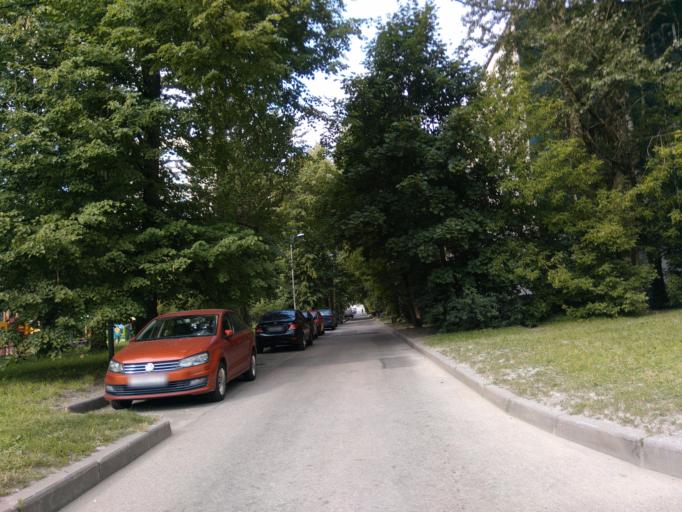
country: RU
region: Leningrad
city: Akademicheskoe
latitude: 60.0226
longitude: 30.3945
